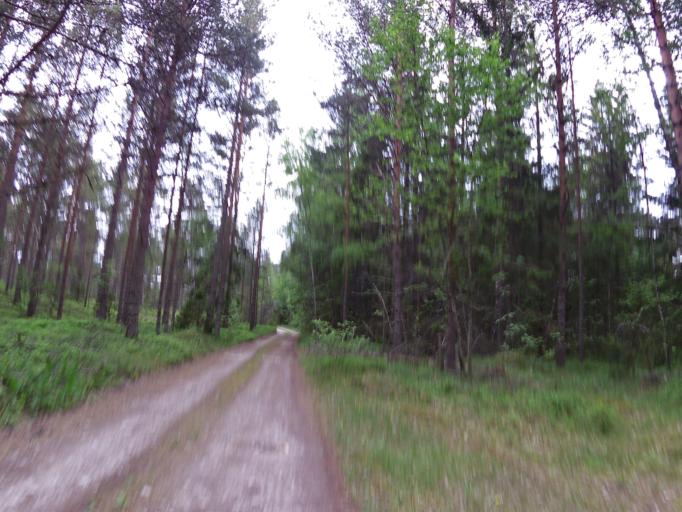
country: EE
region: Harju
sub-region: Paldiski linn
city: Paldiski
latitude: 59.2473
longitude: 23.7477
